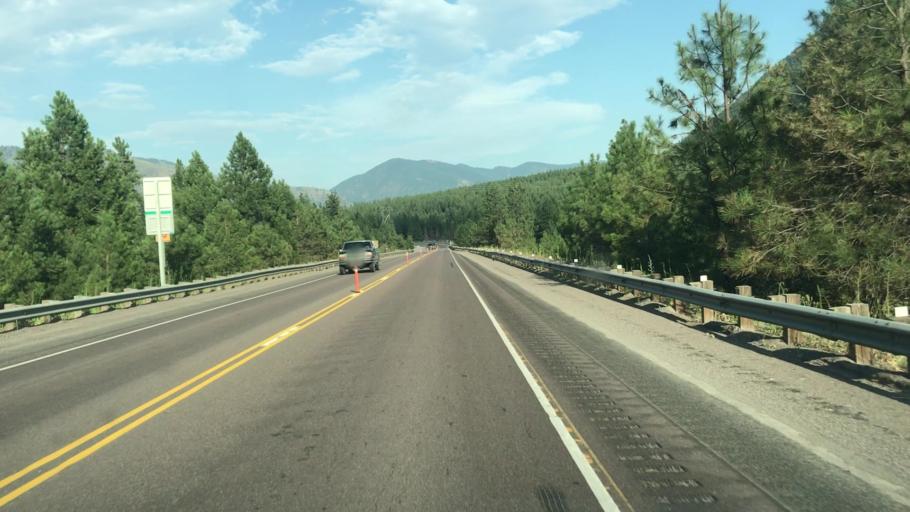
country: US
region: Montana
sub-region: Mineral County
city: Superior
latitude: 47.0183
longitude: -114.6755
